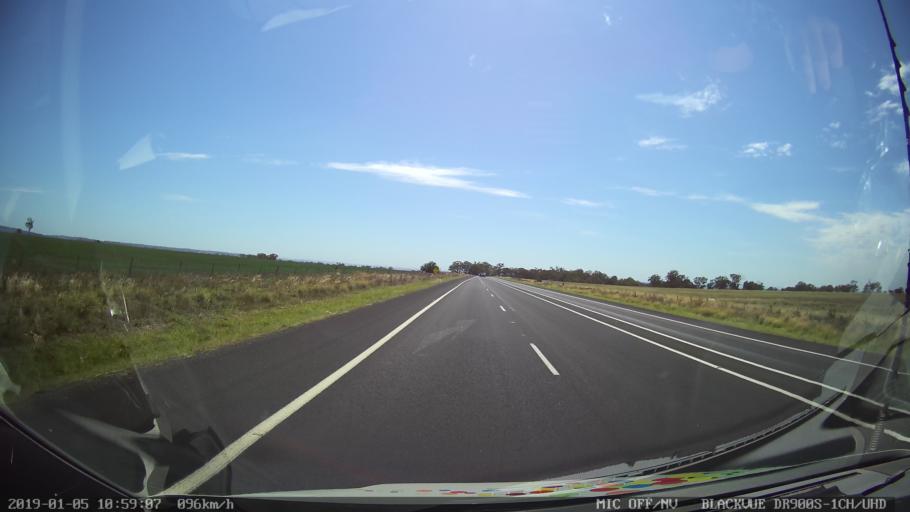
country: AU
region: New South Wales
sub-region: Warrumbungle Shire
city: Coonabarabran
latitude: -31.4163
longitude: 149.1906
